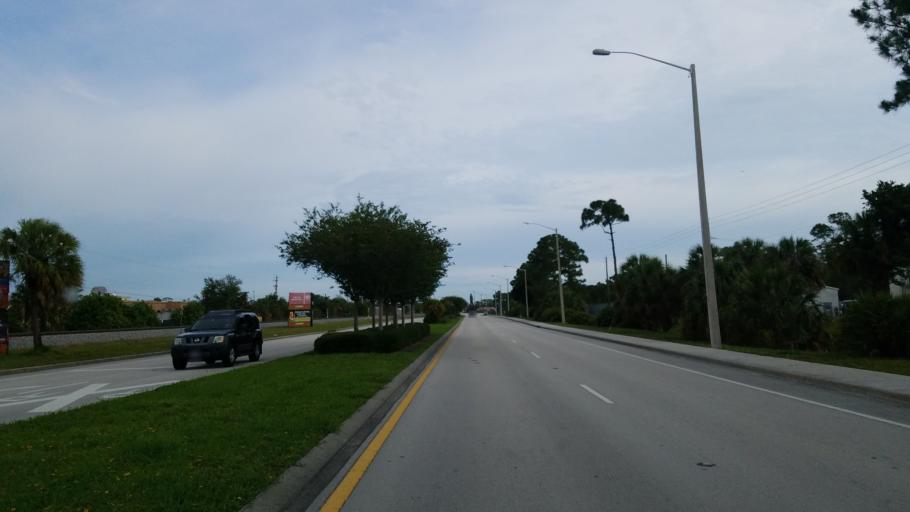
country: US
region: Florida
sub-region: Martin County
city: Stuart
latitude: 27.1779
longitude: -80.2328
